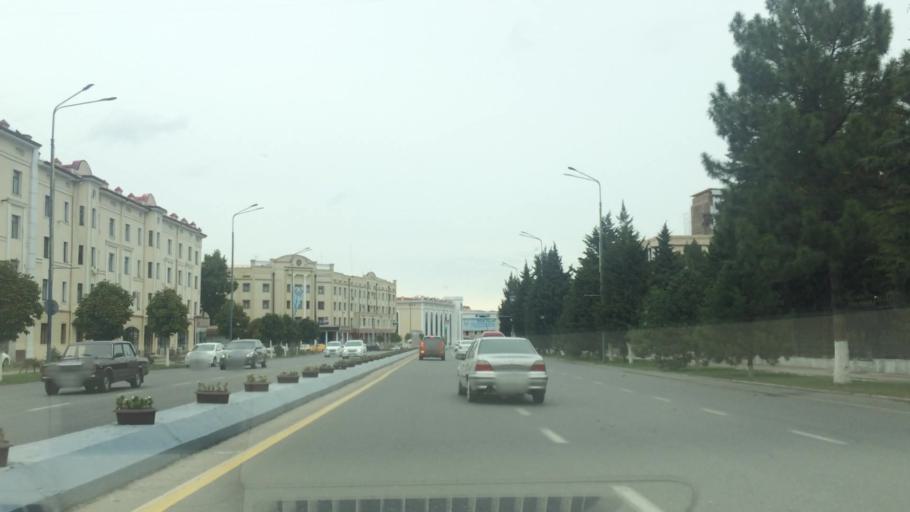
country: UZ
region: Samarqand
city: Samarqand
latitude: 39.6528
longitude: 66.9620
